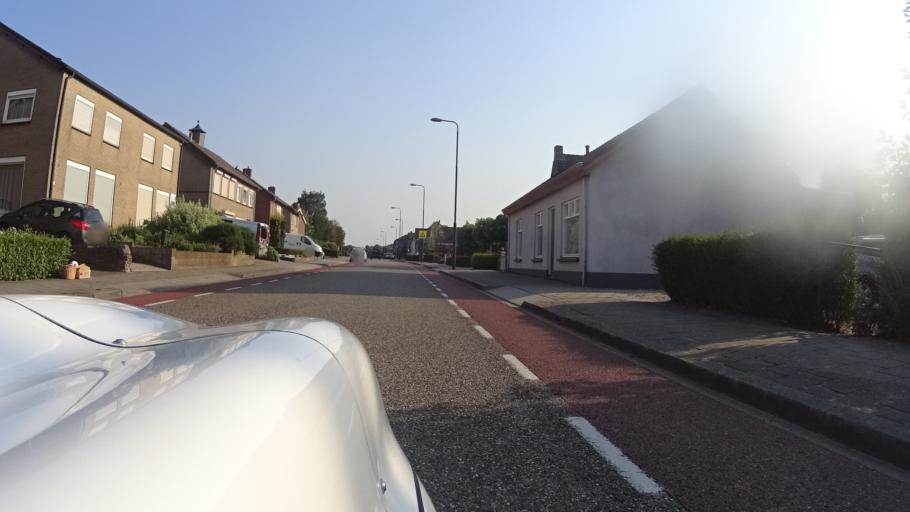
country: NL
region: North Brabant
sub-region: Gemeente Mill en Sint Hubert
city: Wilbertoord
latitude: 51.6908
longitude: 5.7800
